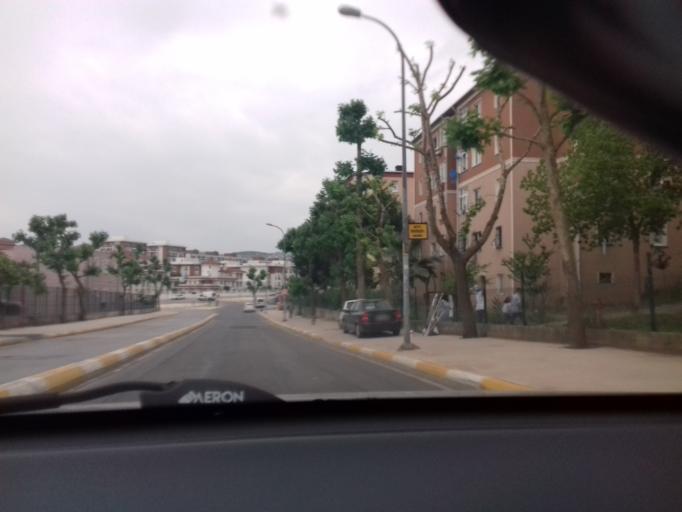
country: TR
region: Istanbul
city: Sultanbeyli
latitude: 40.9331
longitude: 29.2965
